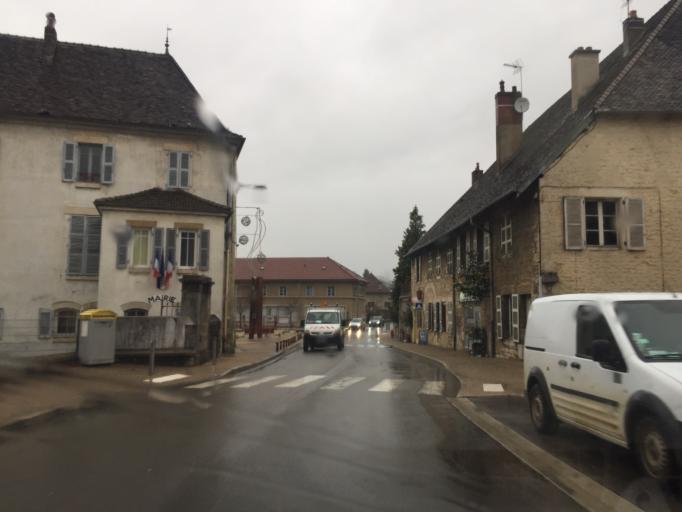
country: FR
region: Franche-Comte
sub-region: Departement du Jura
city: Mouchard
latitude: 46.9766
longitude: 5.7981
